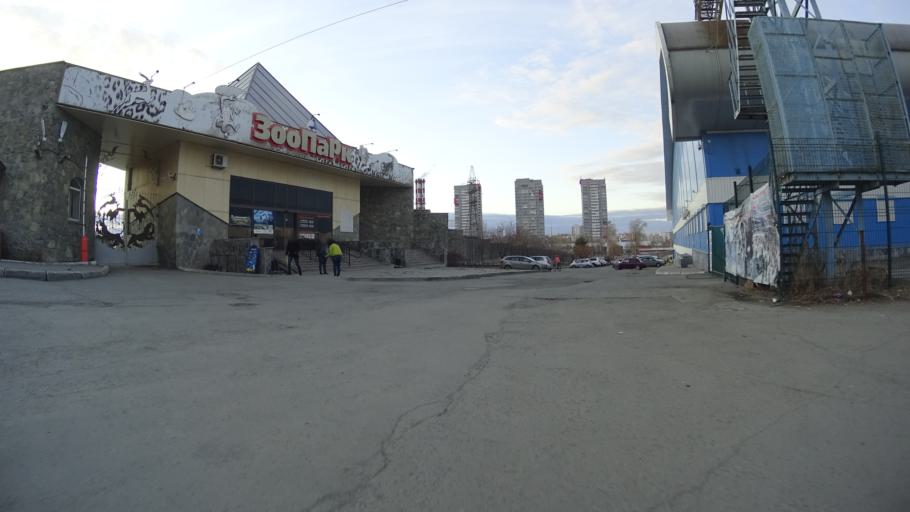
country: RU
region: Chelyabinsk
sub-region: Gorod Chelyabinsk
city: Chelyabinsk
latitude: 55.1678
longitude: 61.3700
